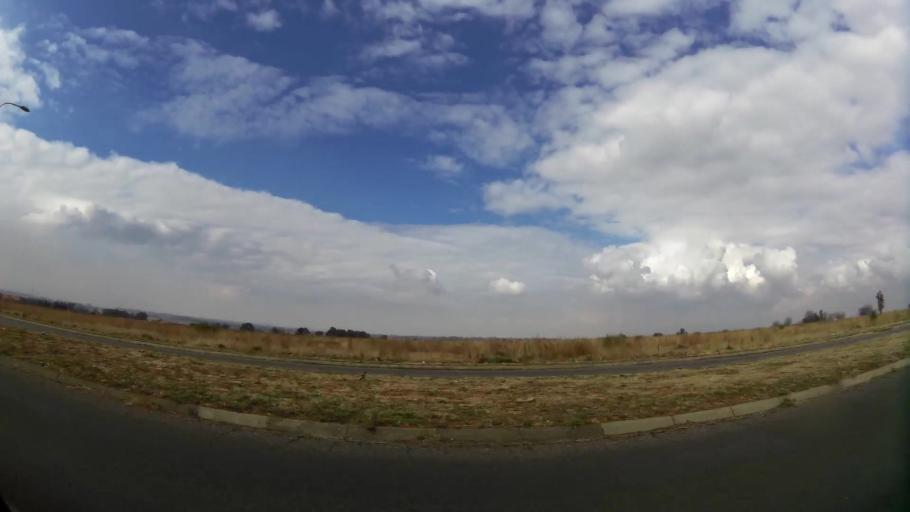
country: ZA
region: Gauteng
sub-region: Sedibeng District Municipality
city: Vanderbijlpark
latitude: -26.7272
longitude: 27.8749
